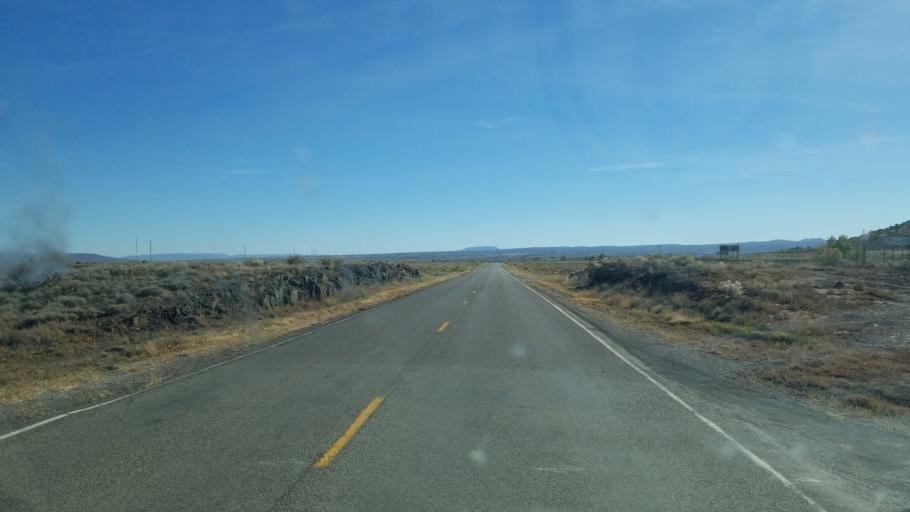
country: US
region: New Mexico
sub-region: Cibola County
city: Milan
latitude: 35.3054
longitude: -107.9880
